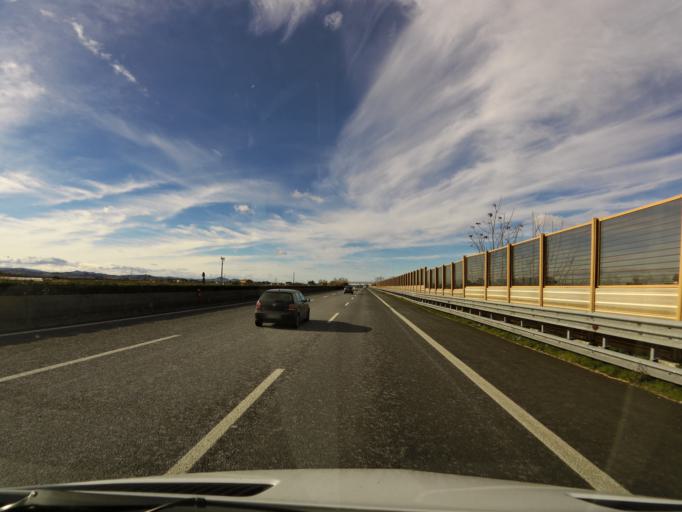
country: IT
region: Emilia-Romagna
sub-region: Forli-Cesena
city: Bagnarola
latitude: 44.1436
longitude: 12.3365
